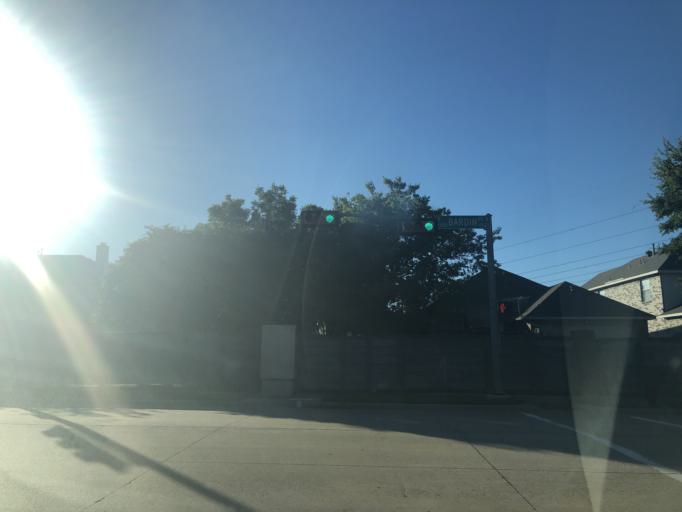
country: US
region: Texas
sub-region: Dallas County
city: Grand Prairie
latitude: 32.6652
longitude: -96.9955
